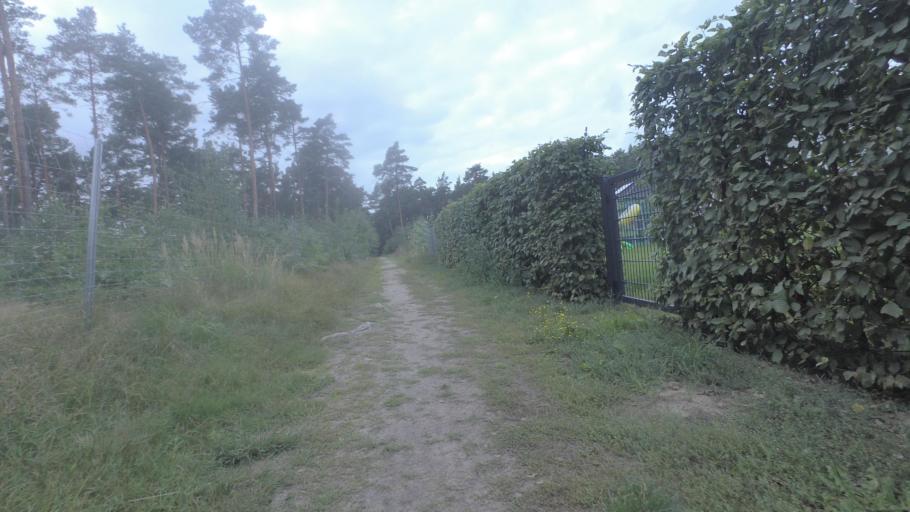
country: DE
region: Brandenburg
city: Ludwigsfelde
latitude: 52.3070
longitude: 13.2207
